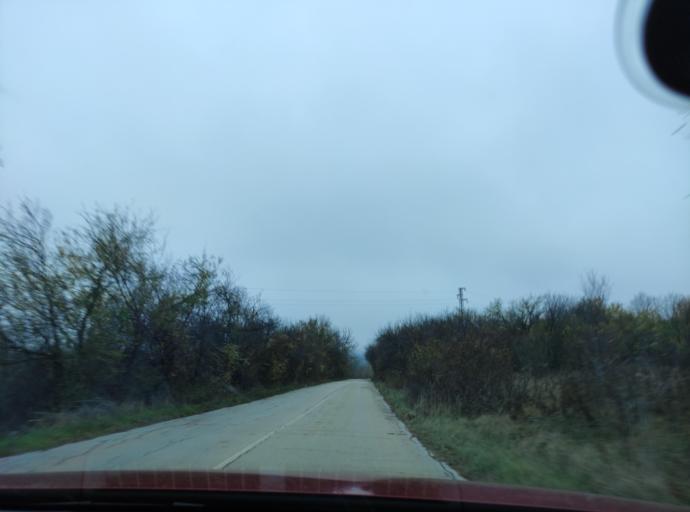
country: BG
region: Lovech
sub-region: Obshtina Yablanitsa
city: Yablanitsa
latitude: 43.0728
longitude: 24.0801
